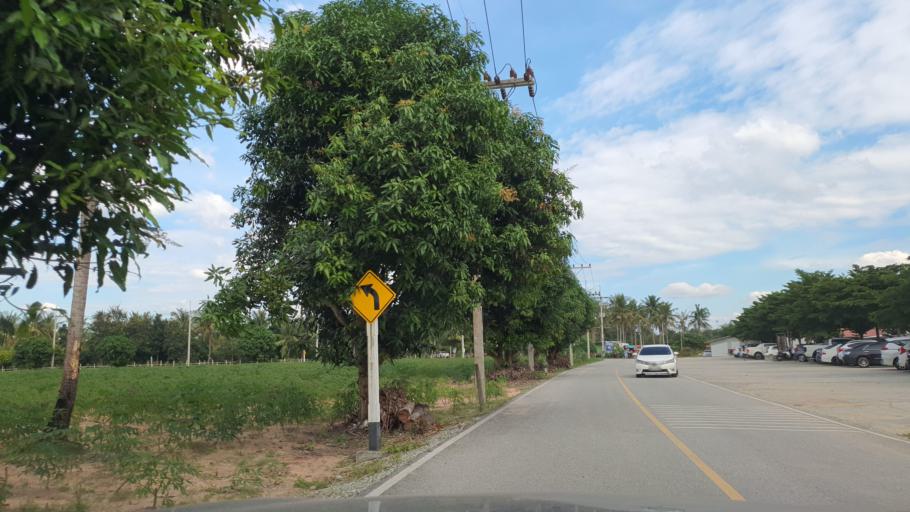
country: TH
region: Chon Buri
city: Bang Lamung
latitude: 12.9735
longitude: 100.9757
